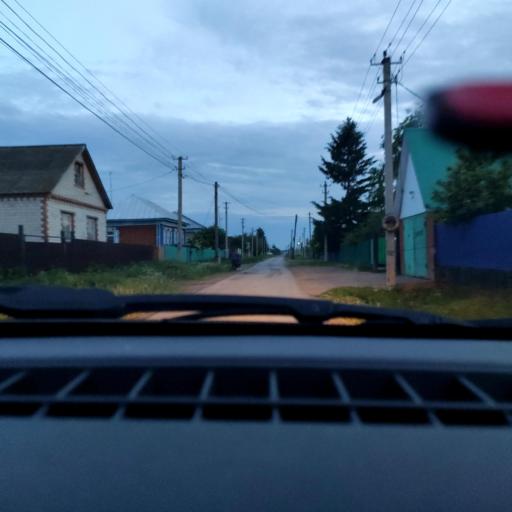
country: RU
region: Bashkortostan
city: Tolbazy
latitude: 54.2918
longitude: 55.8249
